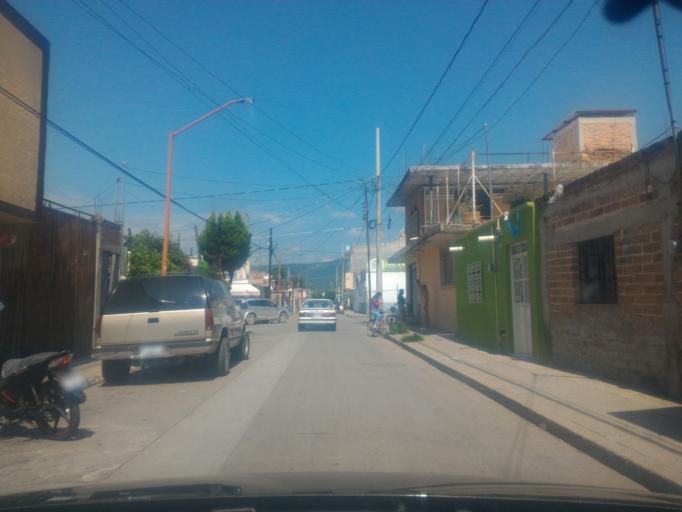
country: MX
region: Guanajuato
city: San Francisco del Rincon
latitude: 21.0081
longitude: -101.8562
